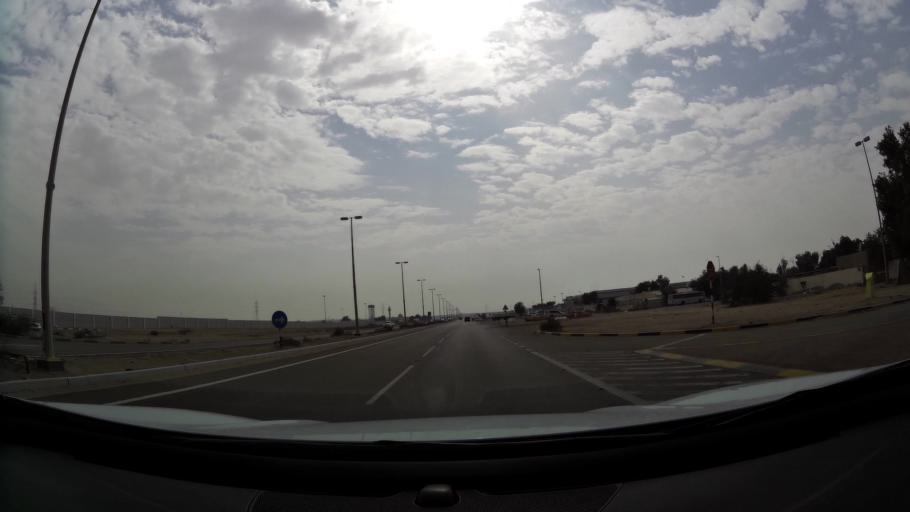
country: AE
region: Abu Dhabi
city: Abu Dhabi
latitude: 24.2891
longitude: 54.6622
